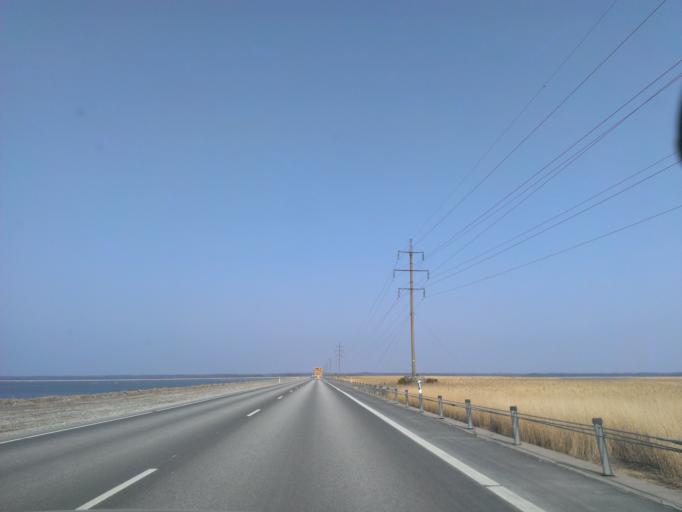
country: EE
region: Saare
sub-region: Orissaare vald
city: Orissaare
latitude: 58.5523
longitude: 23.1416
